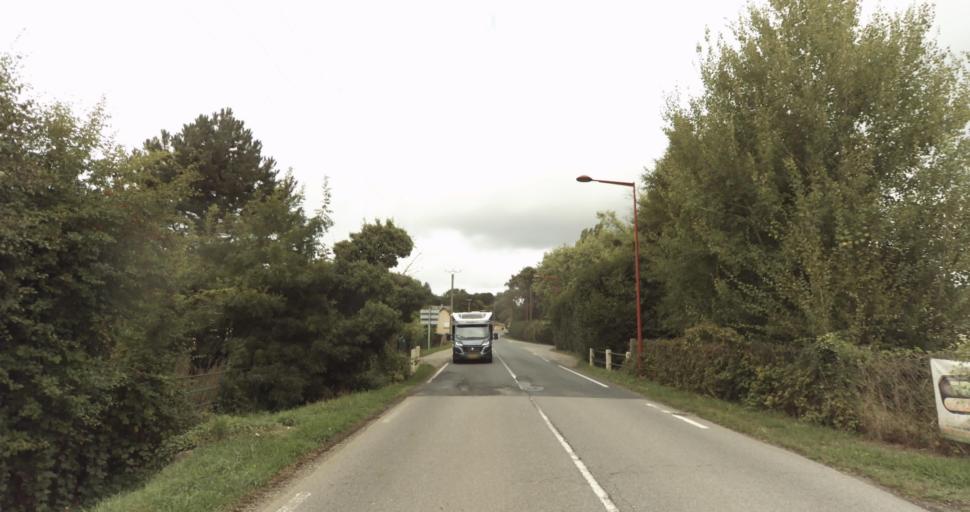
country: FR
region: Lower Normandy
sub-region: Departement de l'Orne
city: Gace
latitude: 48.7997
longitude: 0.2913
